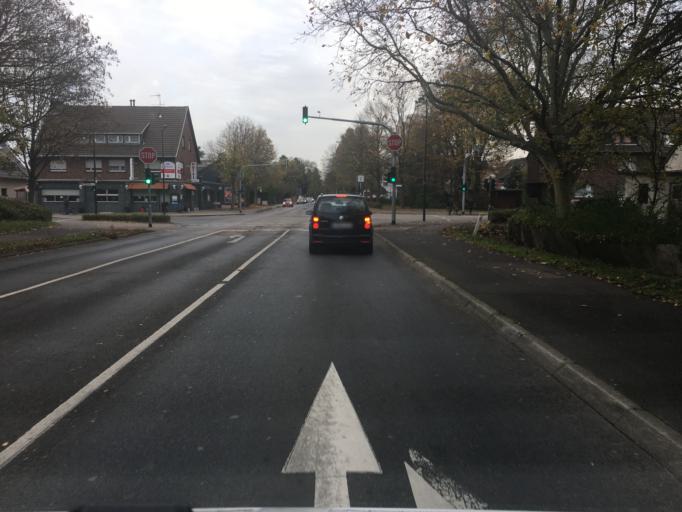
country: DE
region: North Rhine-Westphalia
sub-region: Regierungsbezirk Koln
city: Hurth
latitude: 50.8832
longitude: 6.8844
